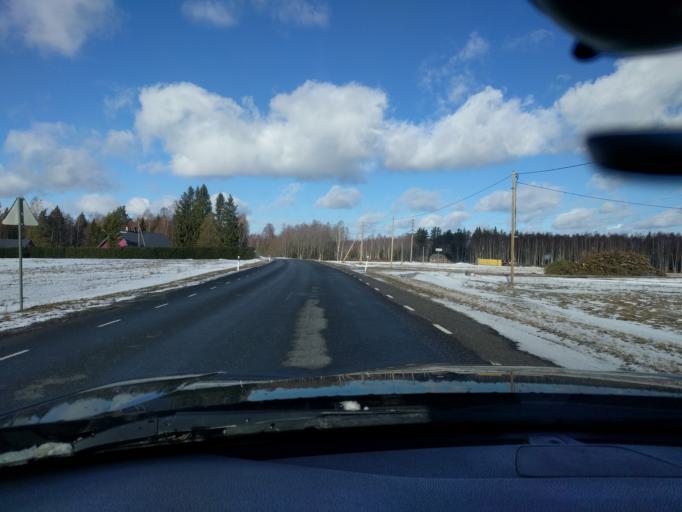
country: EE
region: Harju
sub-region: Anija vald
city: Kehra
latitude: 59.2336
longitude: 25.3855
